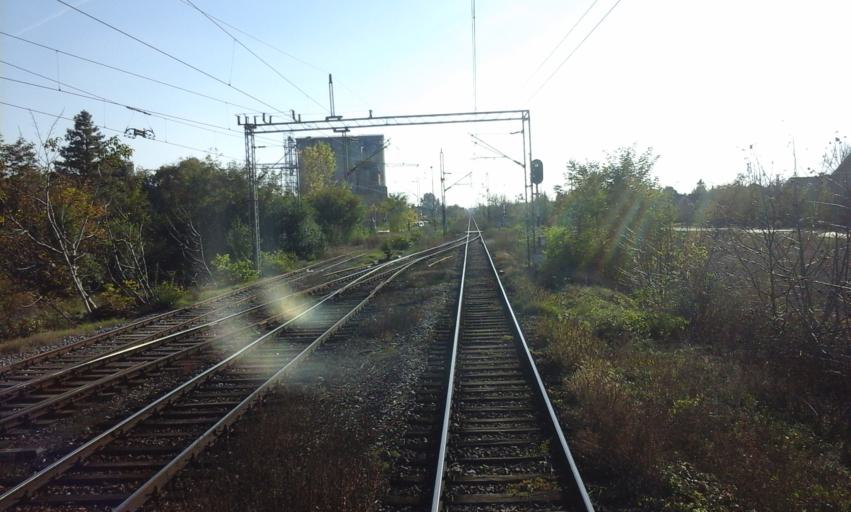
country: RS
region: Autonomna Pokrajina Vojvodina
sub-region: Severnobacki Okrug
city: Backa Topola
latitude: 45.8123
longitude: 19.6487
